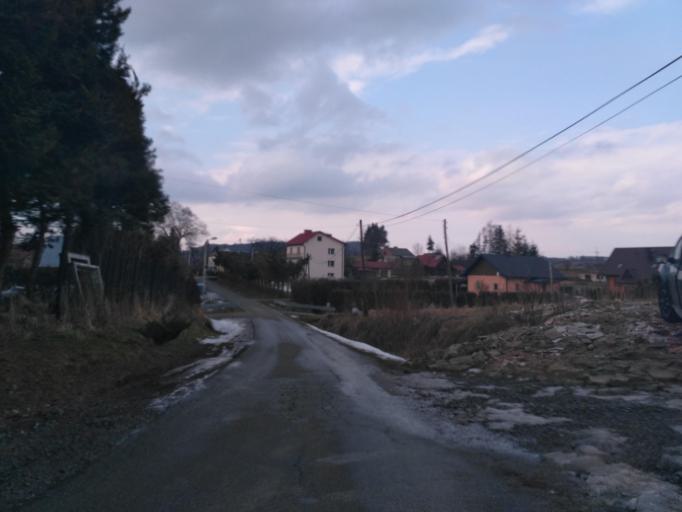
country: PL
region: Subcarpathian Voivodeship
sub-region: Powiat sanocki
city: Strachocina
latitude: 49.6104
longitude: 22.0840
